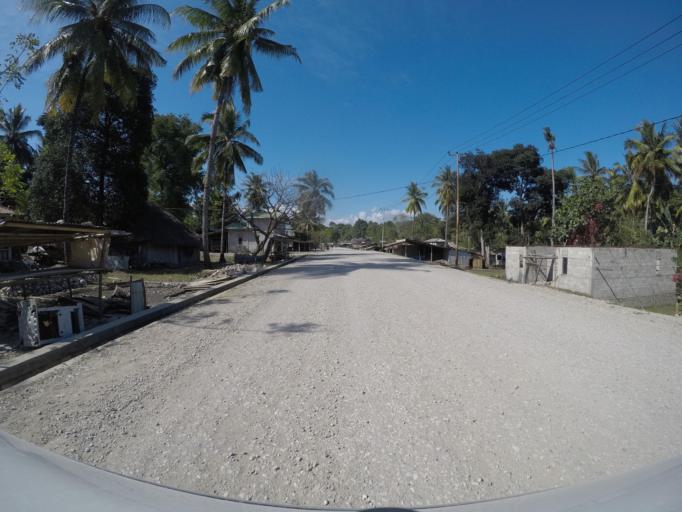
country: TL
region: Viqueque
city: Viqueque
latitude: -8.8382
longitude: 126.5178
